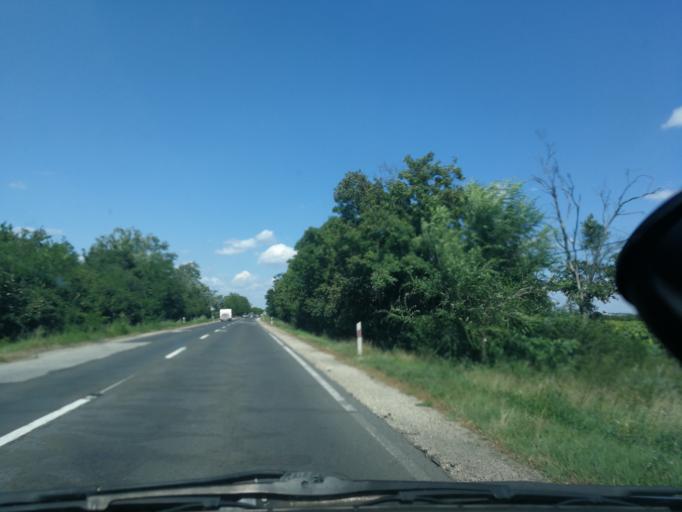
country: HU
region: Pest
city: Tarnok
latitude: 47.3541
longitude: 18.8582
